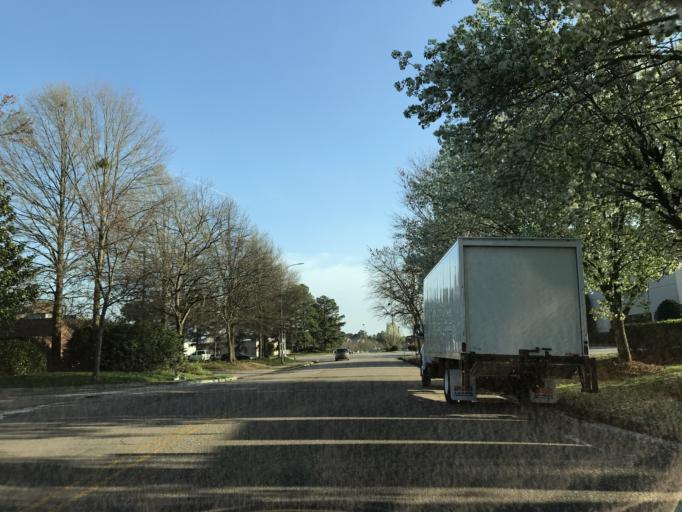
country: US
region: North Carolina
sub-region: Wake County
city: Raleigh
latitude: 35.8507
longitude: -78.5837
